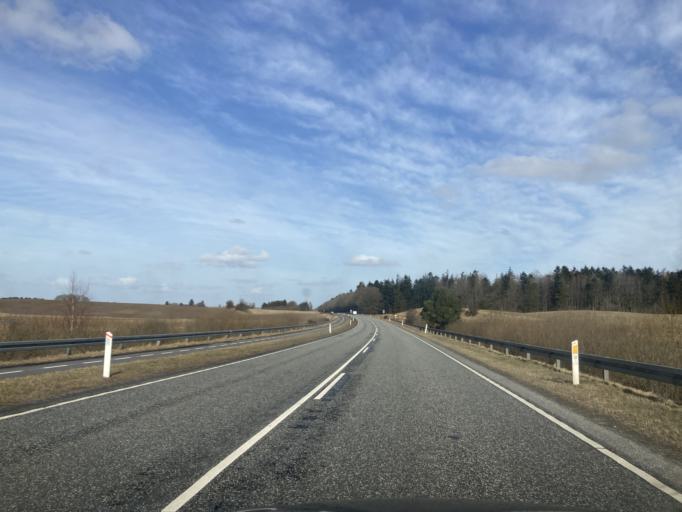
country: DK
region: Central Jutland
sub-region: Hedensted Kommune
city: Torring
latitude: 55.9928
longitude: 9.3880
